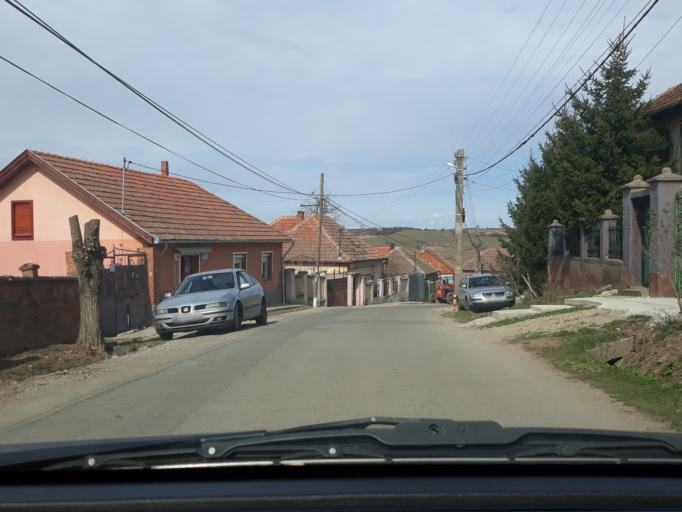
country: RO
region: Bihor
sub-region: Comuna Paleu
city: Paleu
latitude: 47.1174
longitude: 21.9581
